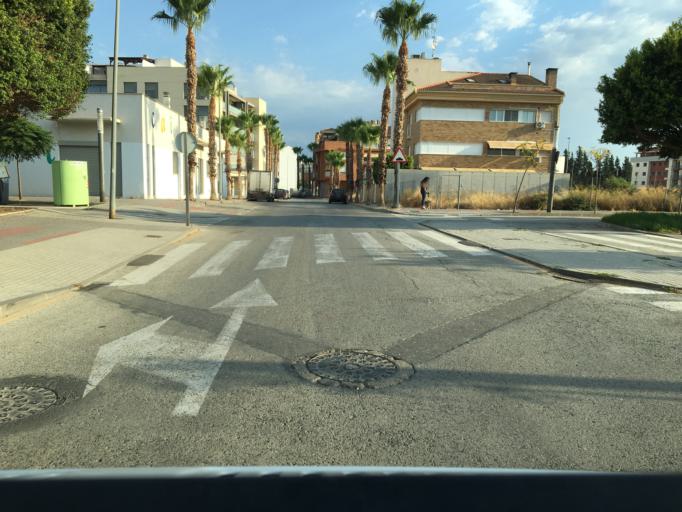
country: ES
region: Murcia
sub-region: Murcia
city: Alcantarilla
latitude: 37.9708
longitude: -1.2057
